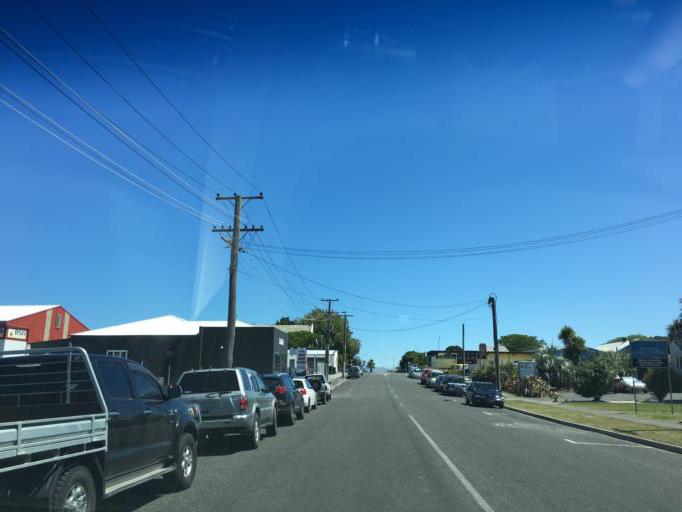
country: NZ
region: Gisborne
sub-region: Gisborne District
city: Gisborne
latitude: -38.6620
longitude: 178.0253
